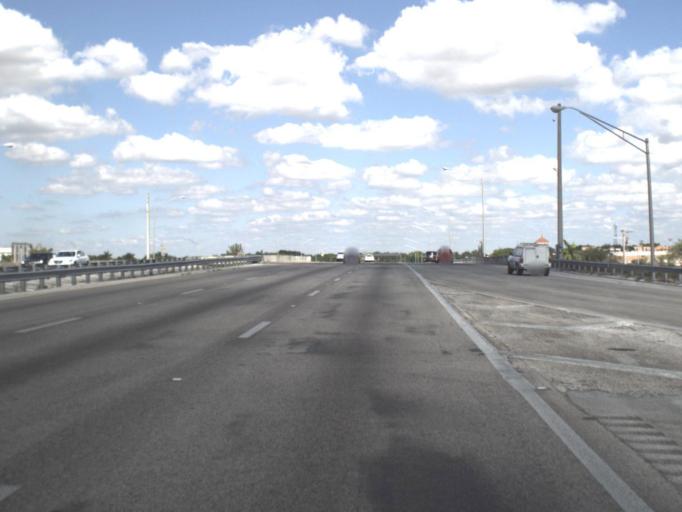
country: US
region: Florida
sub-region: Miami-Dade County
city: The Crossings
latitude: 25.6851
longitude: -80.3889
